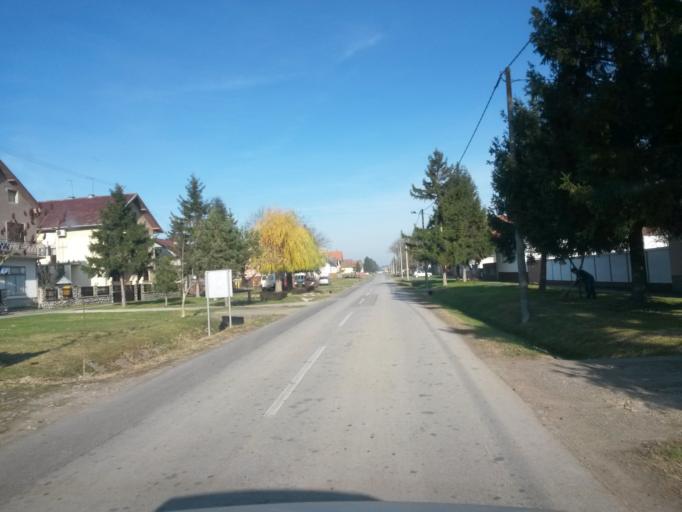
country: HR
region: Vukovarsko-Srijemska
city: Mirkovci
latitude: 45.2407
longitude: 18.8968
